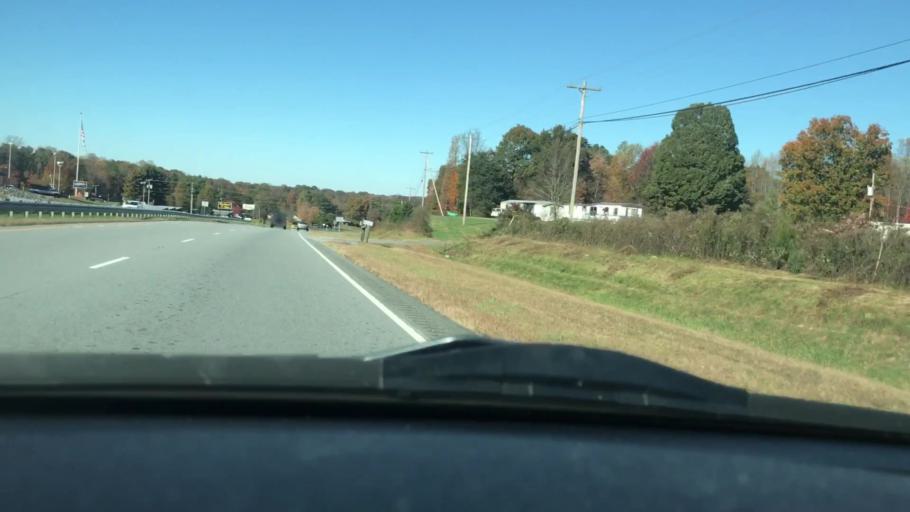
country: US
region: North Carolina
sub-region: Rockingham County
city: Madison
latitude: 36.3525
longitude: -79.9461
